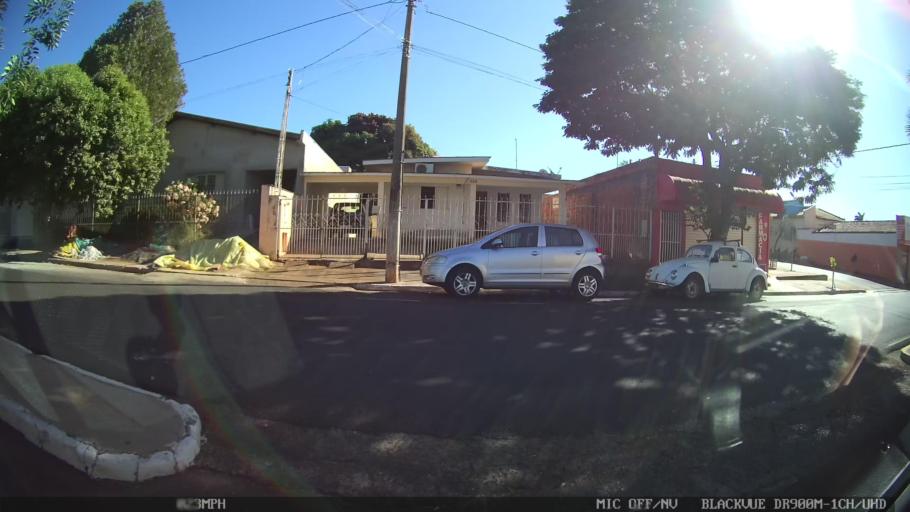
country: BR
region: Sao Paulo
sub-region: Olimpia
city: Olimpia
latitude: -20.7472
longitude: -48.9091
